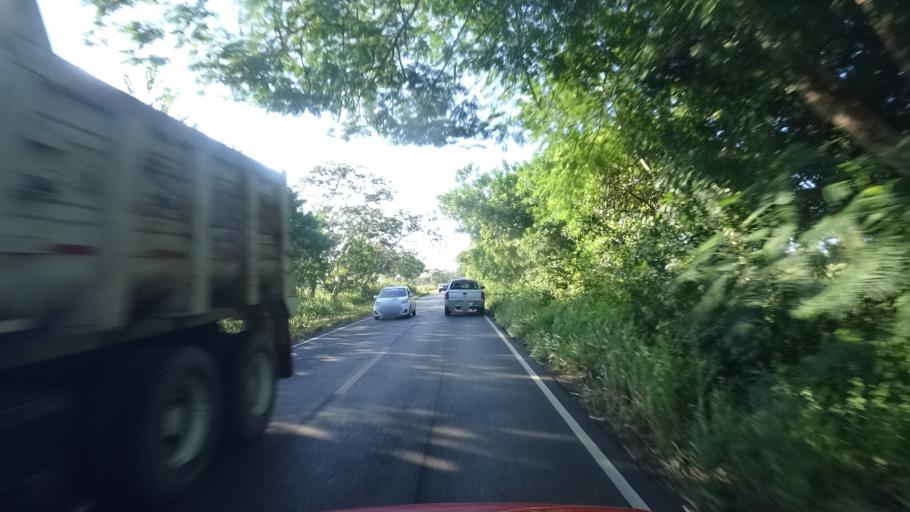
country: MX
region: Yucatan
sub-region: Tizimin
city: Tizimin
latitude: 21.1738
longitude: -88.1586
